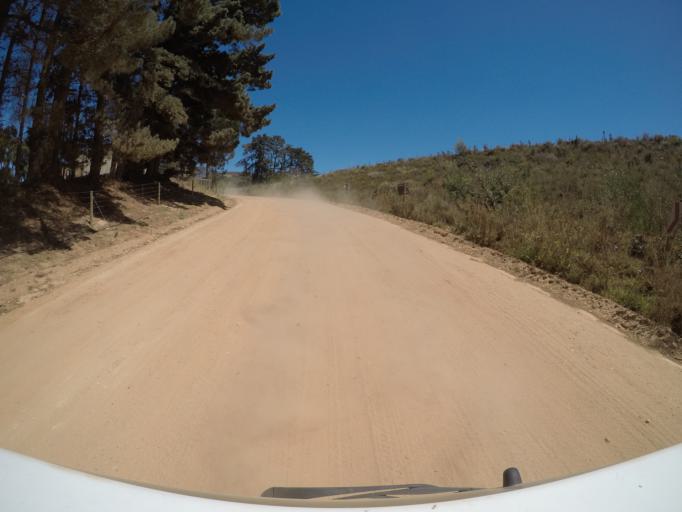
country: ZA
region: Western Cape
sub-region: Overberg District Municipality
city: Grabouw
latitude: -34.2429
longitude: 19.0950
